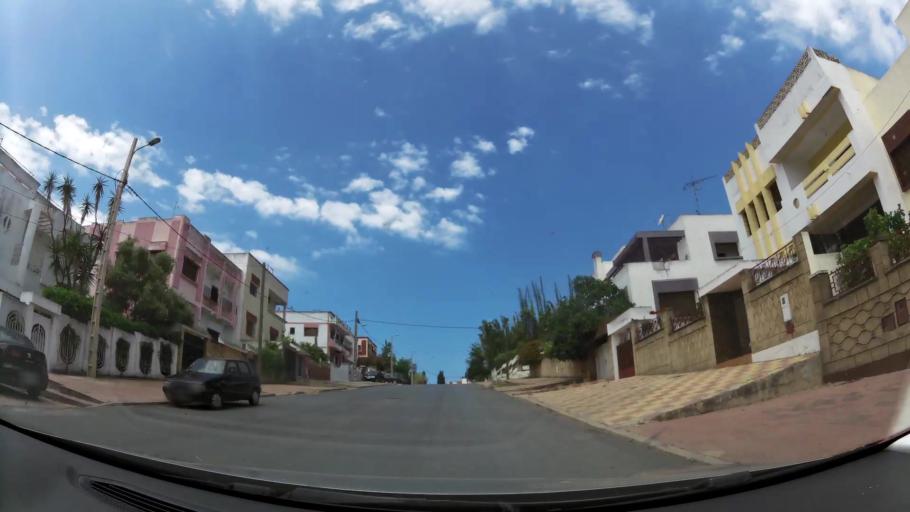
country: MA
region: Gharb-Chrarda-Beni Hssen
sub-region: Kenitra Province
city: Kenitra
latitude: 34.2663
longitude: -6.5931
